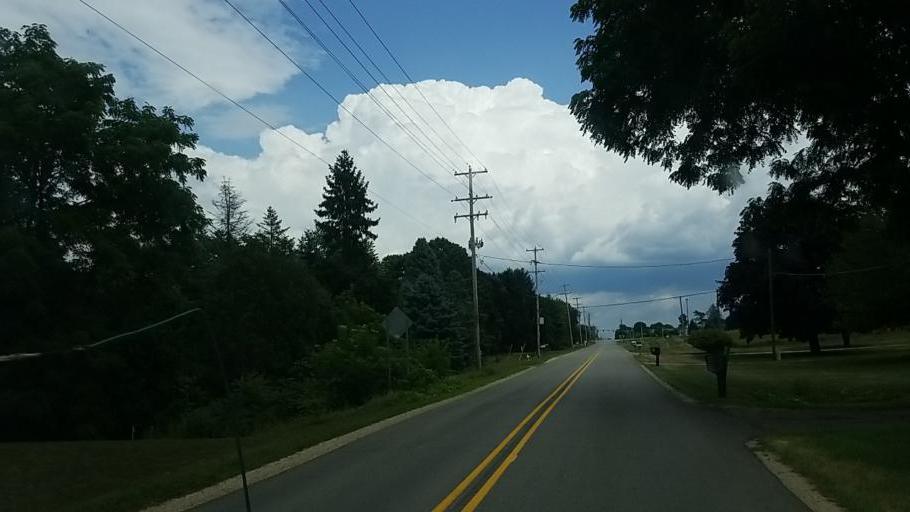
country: US
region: Michigan
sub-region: Kent County
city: Walker
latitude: 43.0160
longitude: -85.7843
